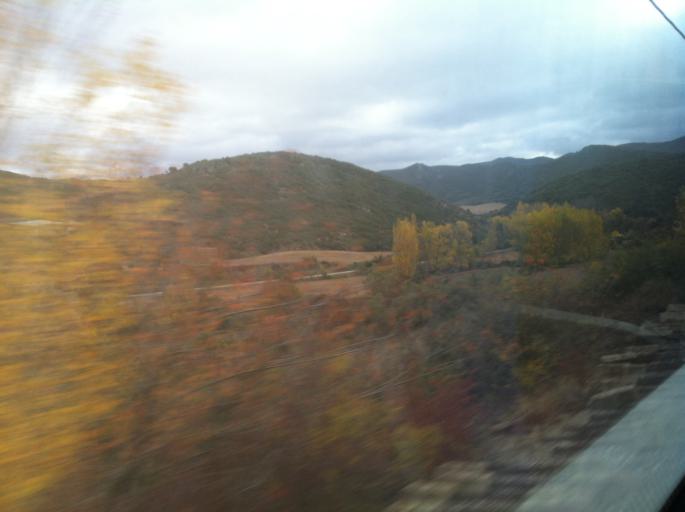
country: ES
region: Castille and Leon
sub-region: Provincia de Burgos
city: Bugedo
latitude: 42.6495
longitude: -2.9990
